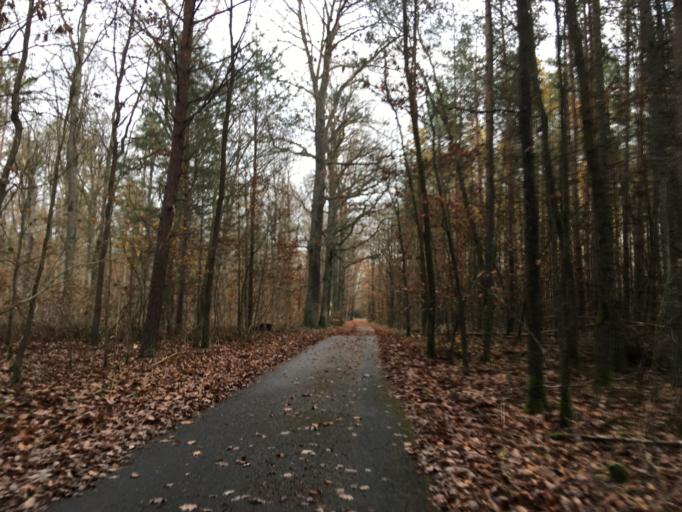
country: DE
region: Brandenburg
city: Tauer
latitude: 51.9200
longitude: 14.4929
